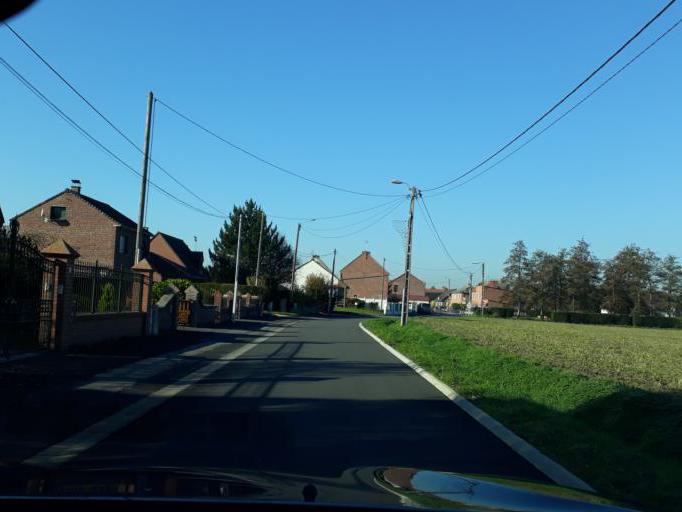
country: FR
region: Nord-Pas-de-Calais
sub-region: Departement du Nord
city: Masny
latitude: 50.3444
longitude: 3.2063
